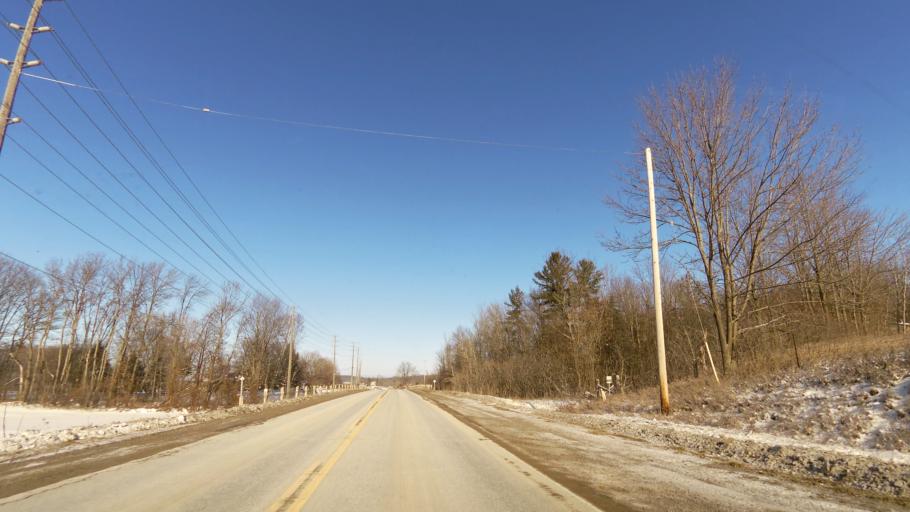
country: CA
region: Ontario
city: Quinte West
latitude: 44.2054
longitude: -77.8220
